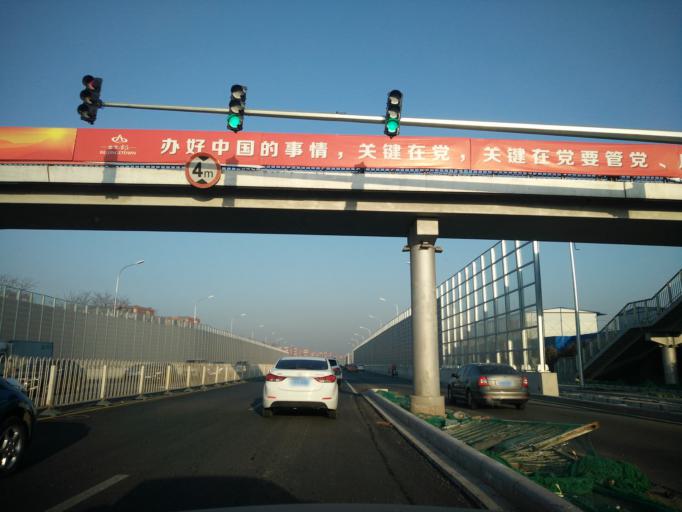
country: CN
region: Beijing
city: Jiugong
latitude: 39.7898
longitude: 116.4811
